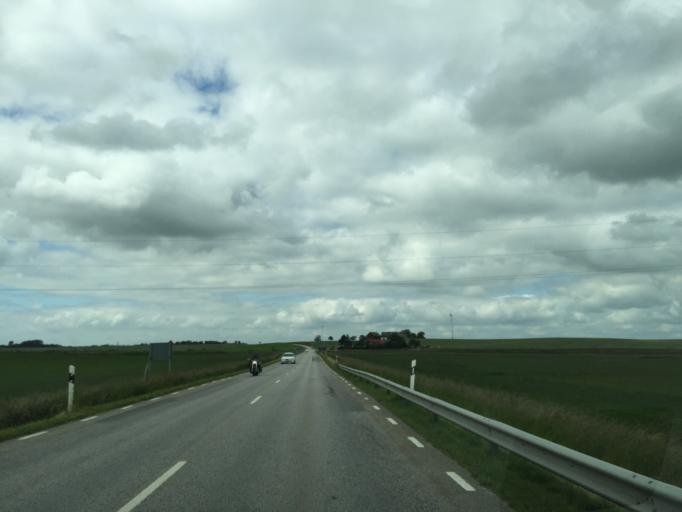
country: SE
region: Skane
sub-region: Svedala Kommun
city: Klagerup
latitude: 55.6146
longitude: 13.2630
